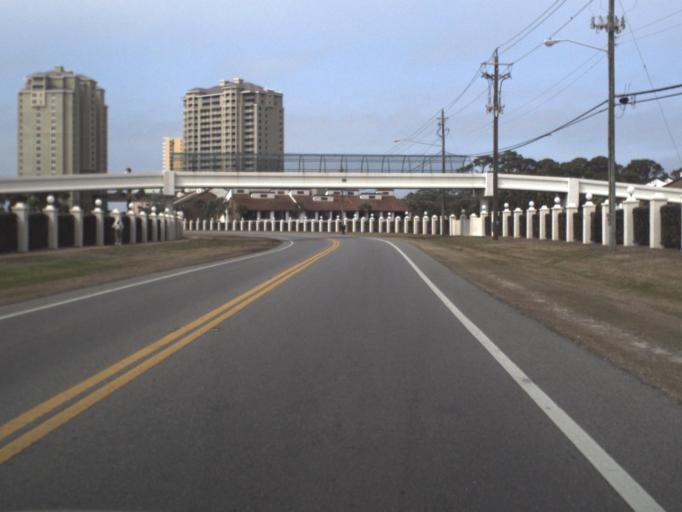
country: US
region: Florida
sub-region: Bay County
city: Panama City Beach
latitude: 30.1858
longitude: -85.8204
